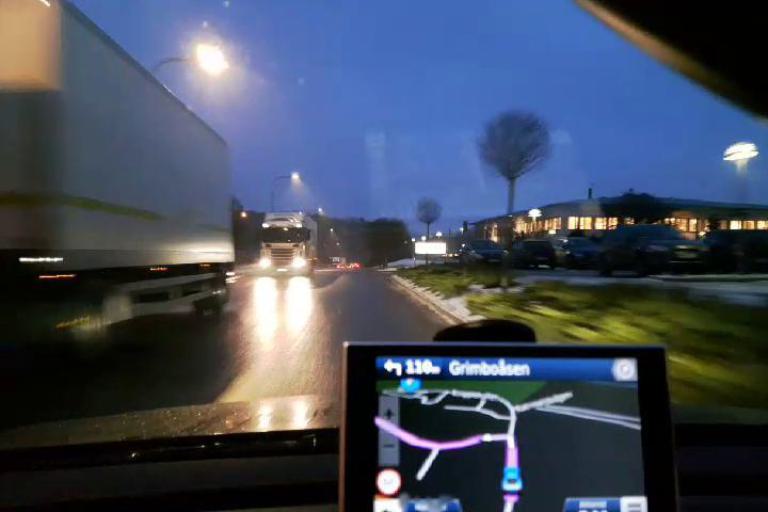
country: SE
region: Vaestra Goetaland
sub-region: Goteborg
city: Goeteborg
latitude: 57.7431
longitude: 11.9419
